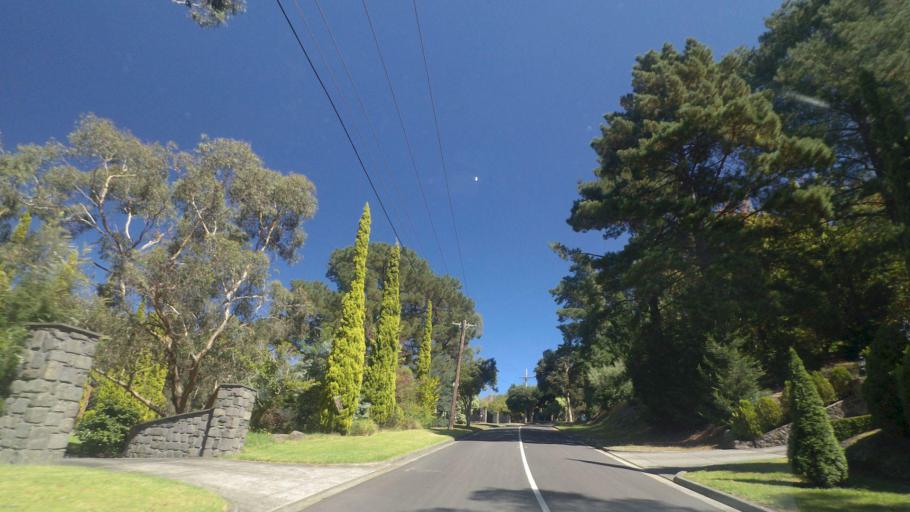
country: AU
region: Victoria
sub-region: Manningham
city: Donvale
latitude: -37.7947
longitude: 145.1898
